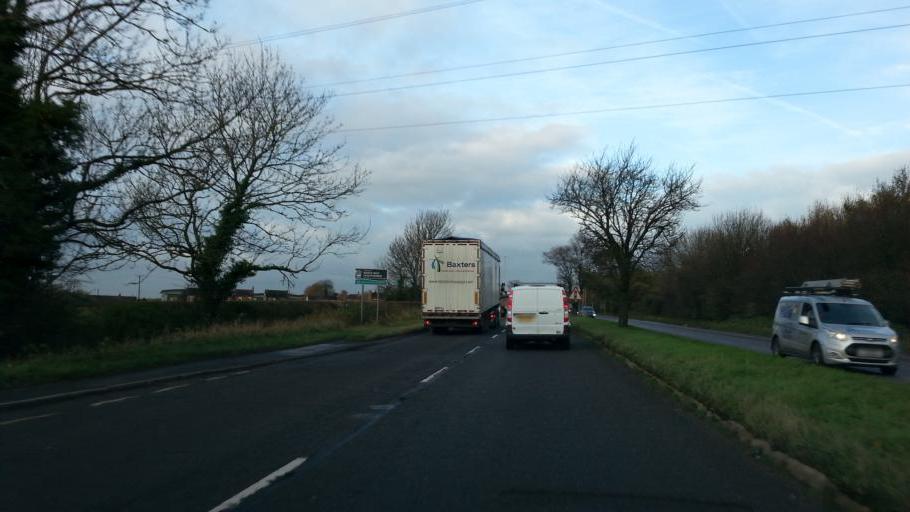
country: GB
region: England
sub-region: Leicestershire
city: Markfield
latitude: 52.7021
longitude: -1.3187
